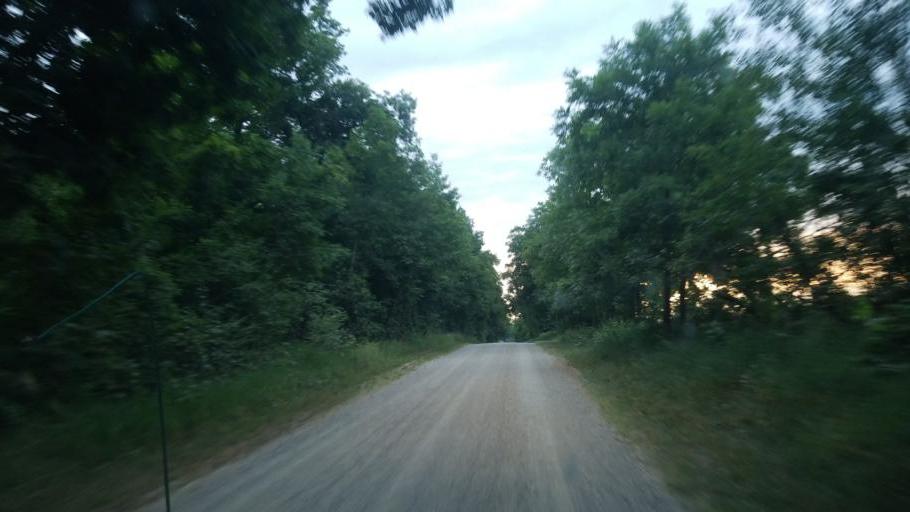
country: US
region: Ohio
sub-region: Defiance County
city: Hicksville
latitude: 41.3287
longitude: -84.8241
